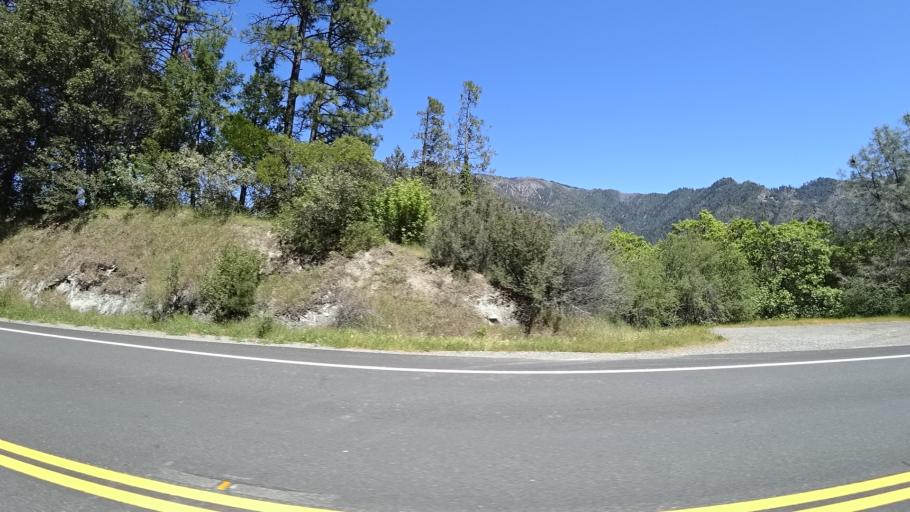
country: US
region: California
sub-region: Humboldt County
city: Willow Creek
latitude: 40.8071
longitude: -123.4717
